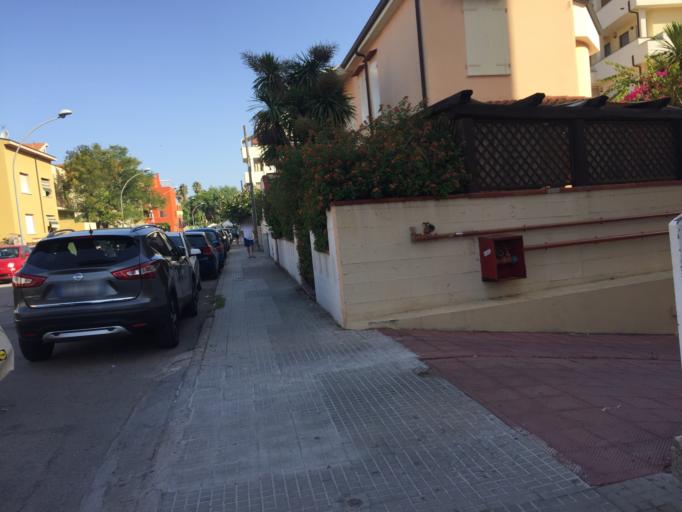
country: IT
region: Sardinia
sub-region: Provincia di Sassari
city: Alghero
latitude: 40.5754
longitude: 8.3174
